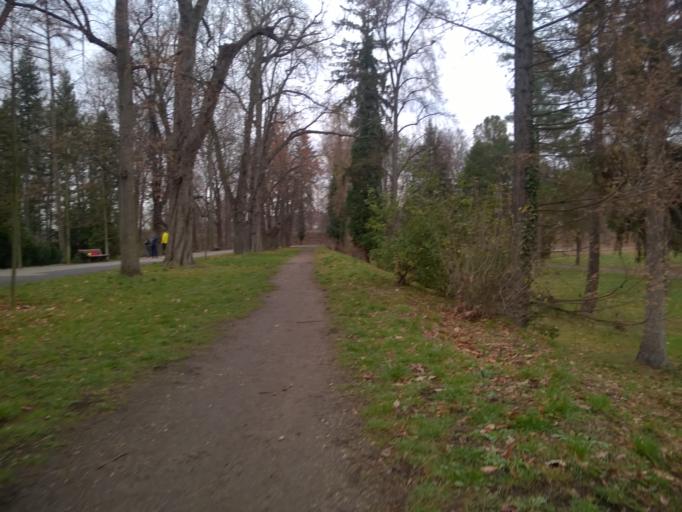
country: CZ
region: Praha
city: Prague
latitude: 50.1065
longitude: 14.4154
